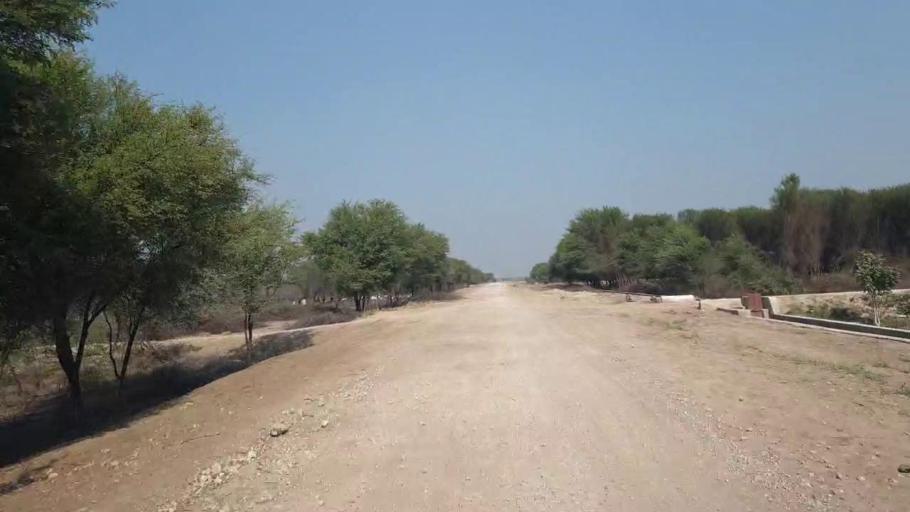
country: PK
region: Sindh
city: Mirwah Gorchani
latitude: 25.3574
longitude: 68.9317
